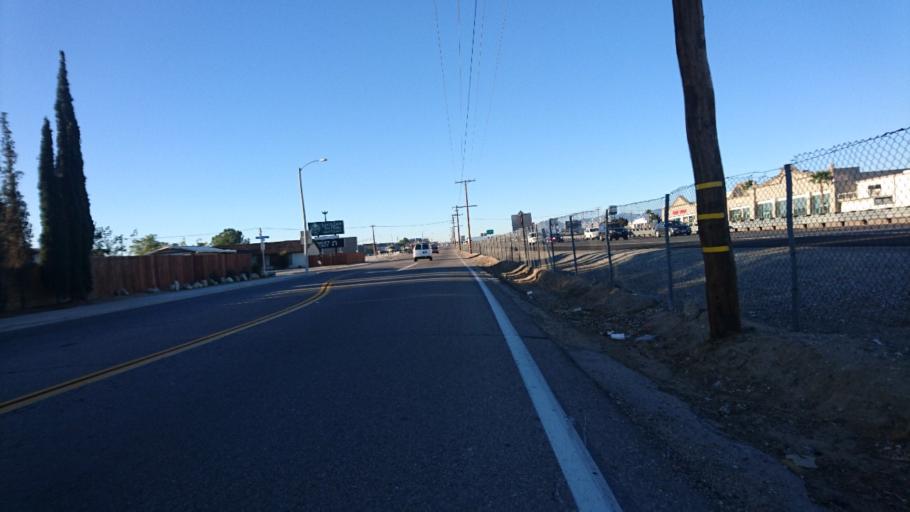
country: US
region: California
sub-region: San Bernardino County
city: Mountain View Acres
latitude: 34.5017
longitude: -117.3248
